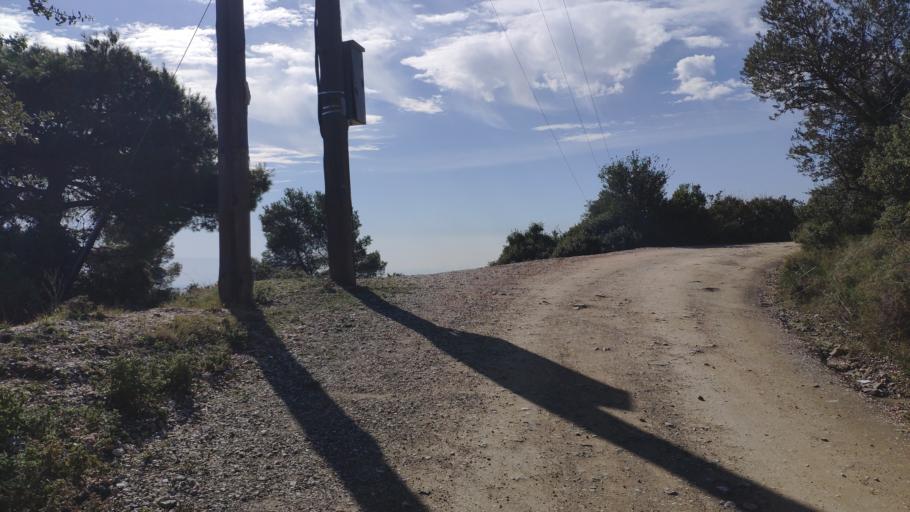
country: GR
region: Attica
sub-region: Nomarchia Anatolikis Attikis
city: Thrakomakedones
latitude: 38.1468
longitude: 23.7710
